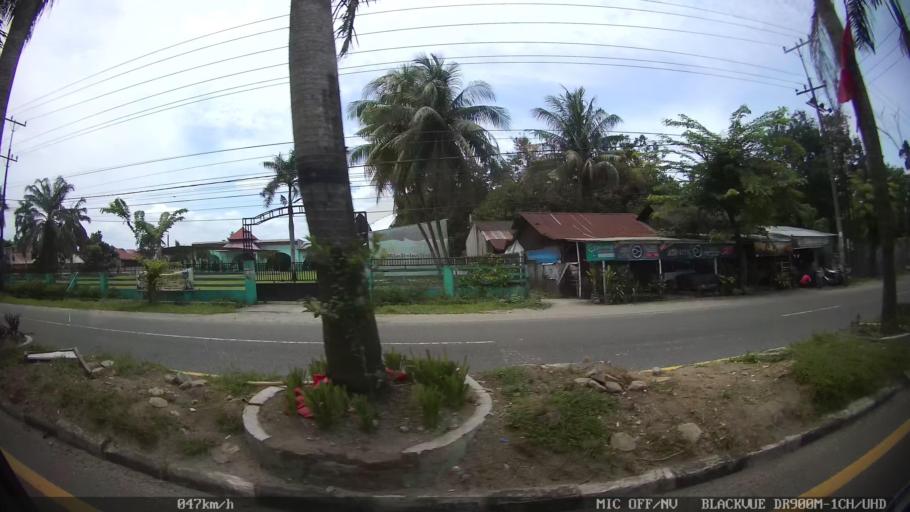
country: ID
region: North Sumatra
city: Sunggal
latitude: 3.5213
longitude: 98.6218
